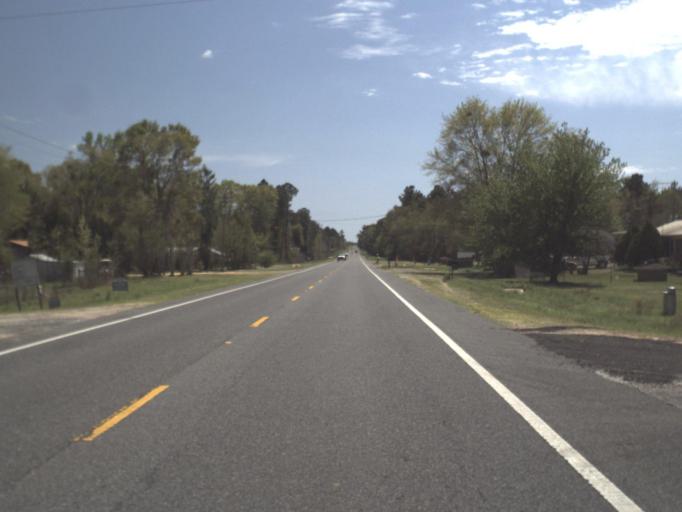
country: US
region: Alabama
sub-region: Geneva County
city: Geneva
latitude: 30.9031
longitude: -85.9560
